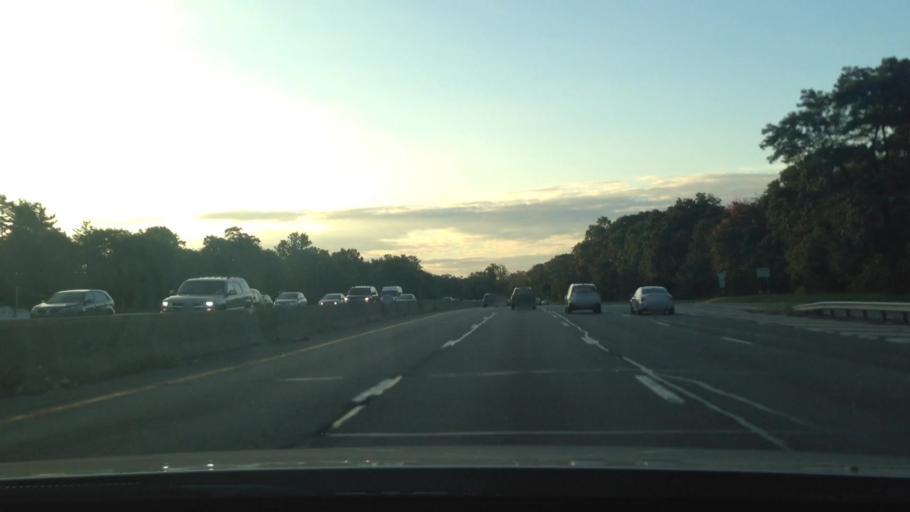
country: US
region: New York
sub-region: Nassau County
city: North Valley Stream
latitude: 40.6823
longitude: -73.7061
